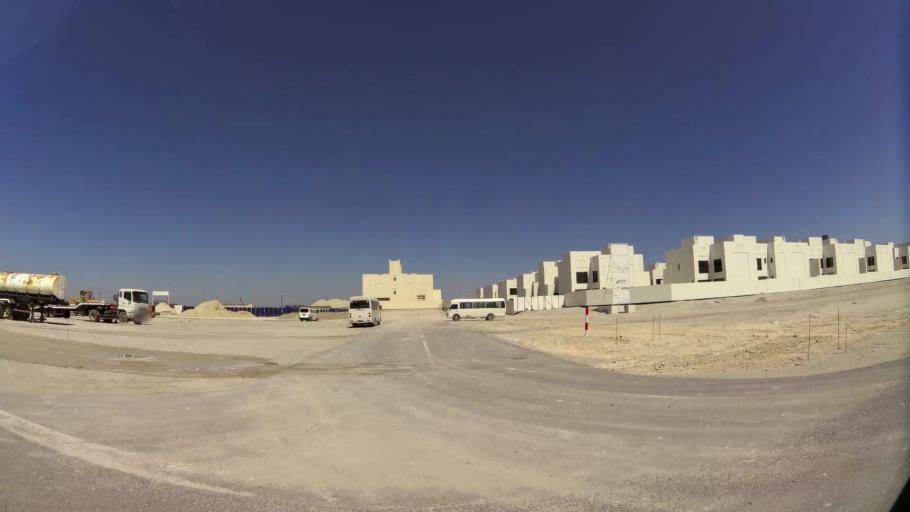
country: BH
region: Muharraq
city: Al Muharraq
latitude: 26.3005
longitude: 50.6316
